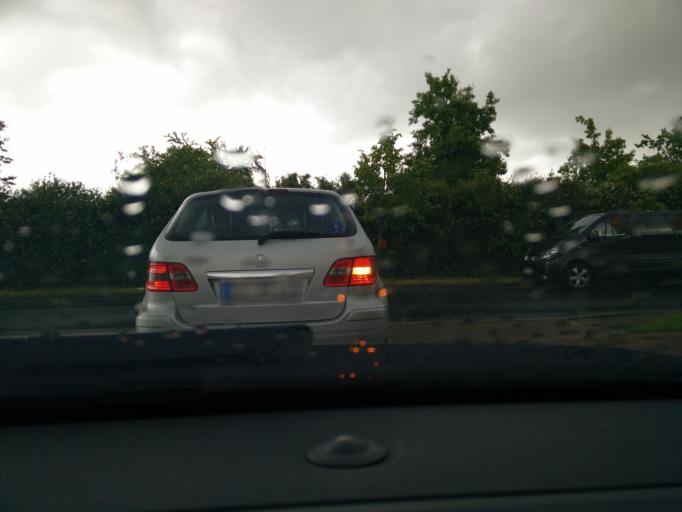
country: DE
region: Saxony
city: Grimma
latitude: 51.2550
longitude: 12.7277
